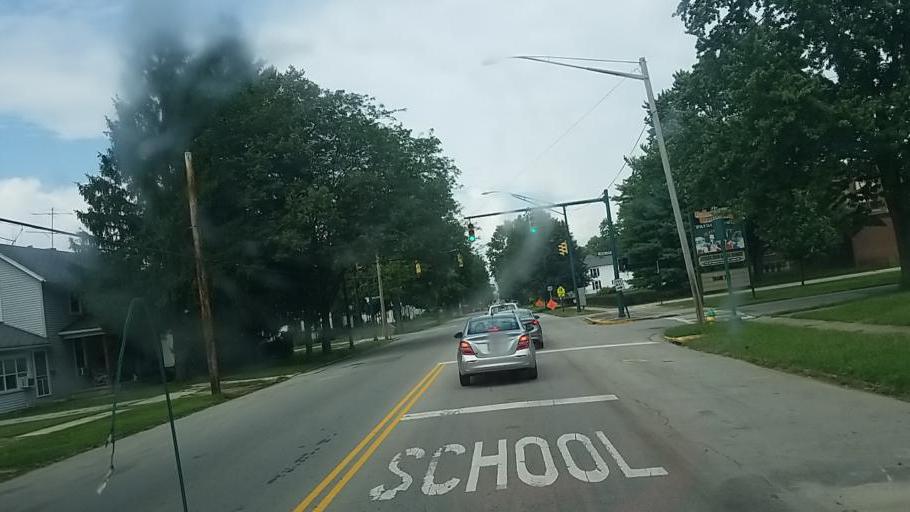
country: US
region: Ohio
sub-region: Champaign County
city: Urbana
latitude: 40.0984
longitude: -83.7535
